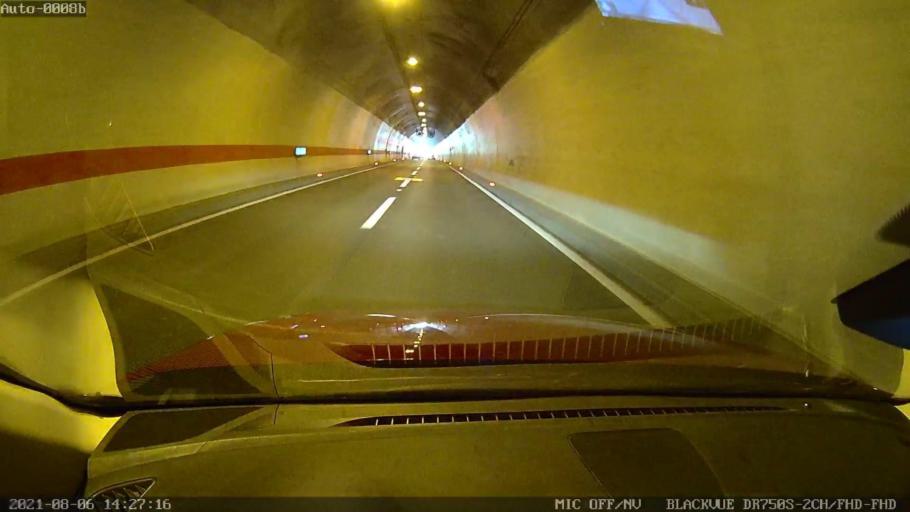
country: HR
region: Primorsko-Goranska
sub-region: Grad Delnice
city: Delnice
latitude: 45.3430
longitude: 14.7489
